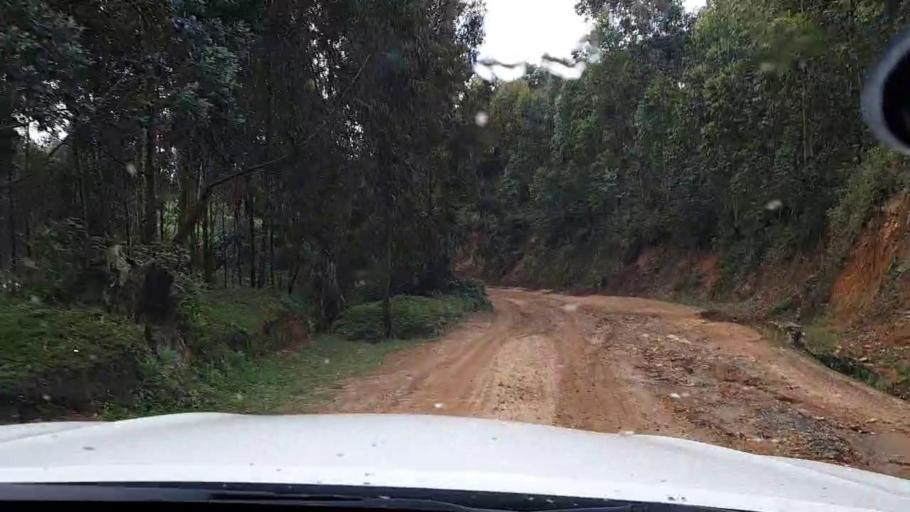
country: RW
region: Western Province
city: Kibuye
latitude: -2.2519
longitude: 29.3456
